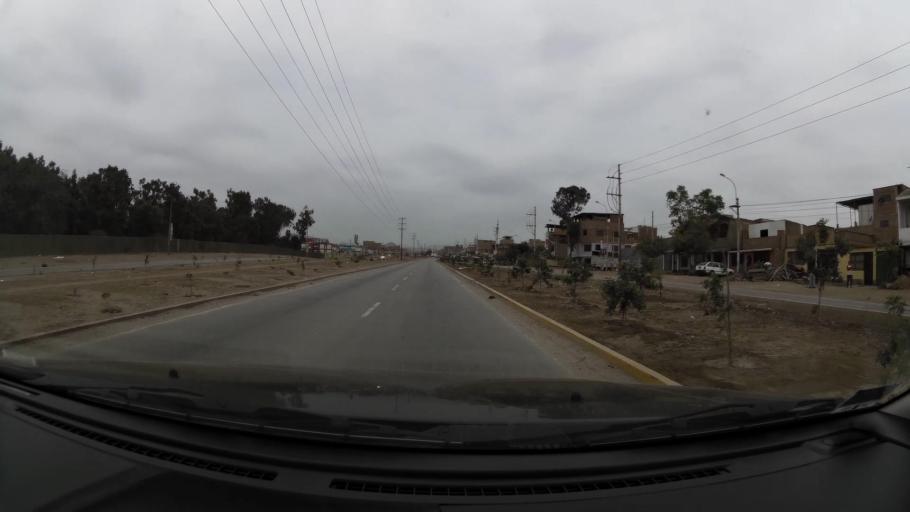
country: PE
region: Lima
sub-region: Lima
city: Surco
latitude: -12.2076
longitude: -76.9561
